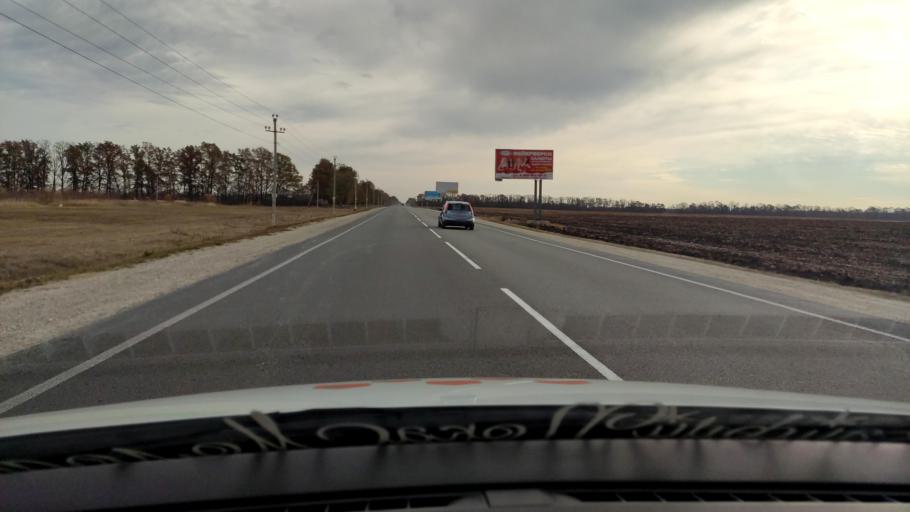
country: RU
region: Voronezj
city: Ramon'
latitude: 51.9292
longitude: 39.2300
